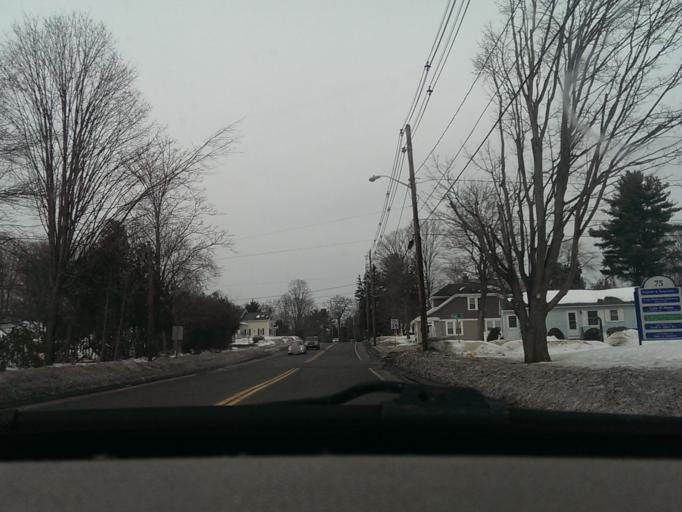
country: US
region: Massachusetts
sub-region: Hampden County
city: East Longmeadow
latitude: 42.0678
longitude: -72.5146
